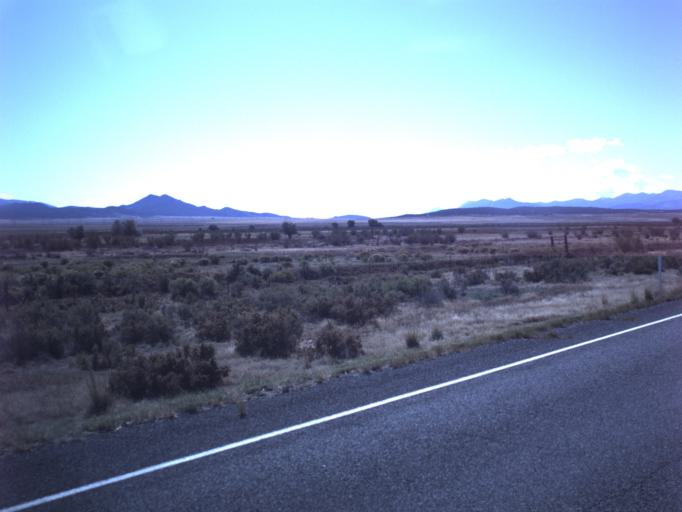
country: US
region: Utah
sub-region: Juab County
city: Nephi
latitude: 39.5135
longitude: -111.9454
